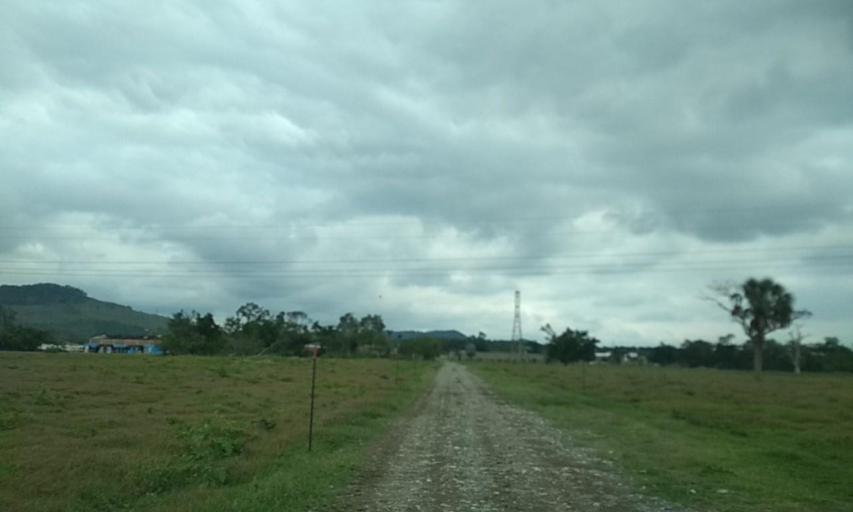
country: MX
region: Veracruz
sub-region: Papantla
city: El Chote
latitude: 20.3922
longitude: -97.3404
